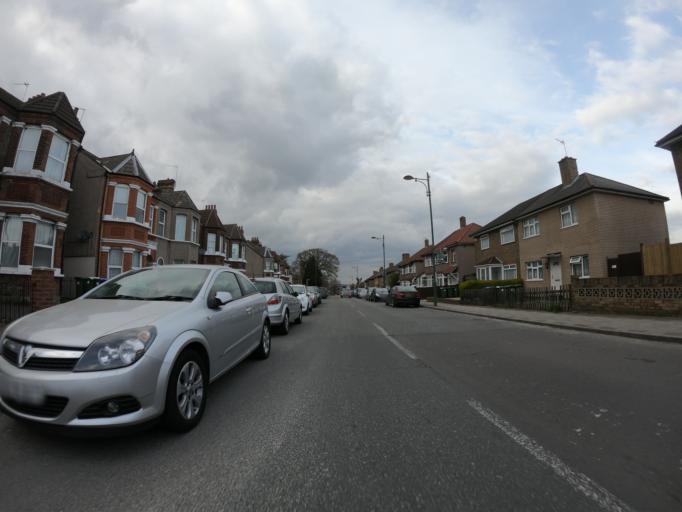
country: GB
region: England
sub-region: Greater London
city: Erith
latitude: 51.4756
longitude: 0.1630
